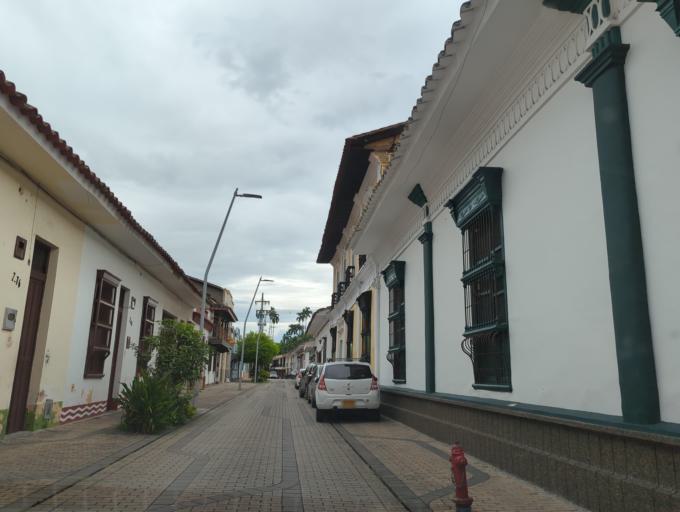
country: CO
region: Valle del Cauca
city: Buga
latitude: 3.8964
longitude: -76.3019
